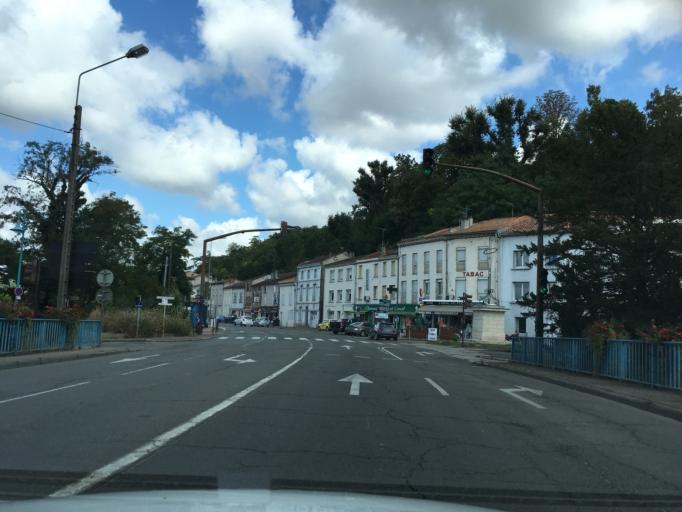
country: FR
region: Aquitaine
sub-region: Departement du Lot-et-Garonne
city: Le Passage
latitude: 44.2091
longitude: 0.6114
